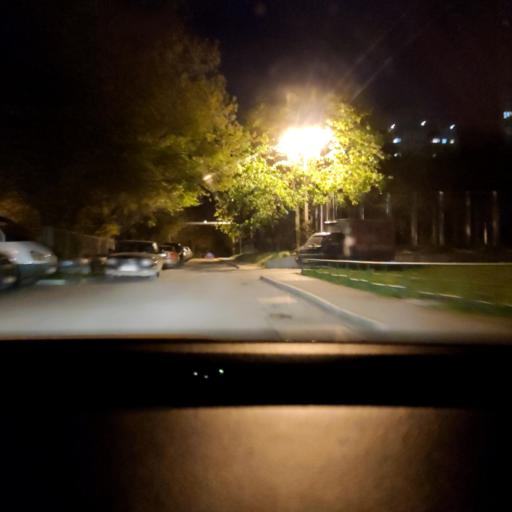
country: RU
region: Moskovskaya
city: Dolgoprudnyy
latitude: 55.9495
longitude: 37.4947
